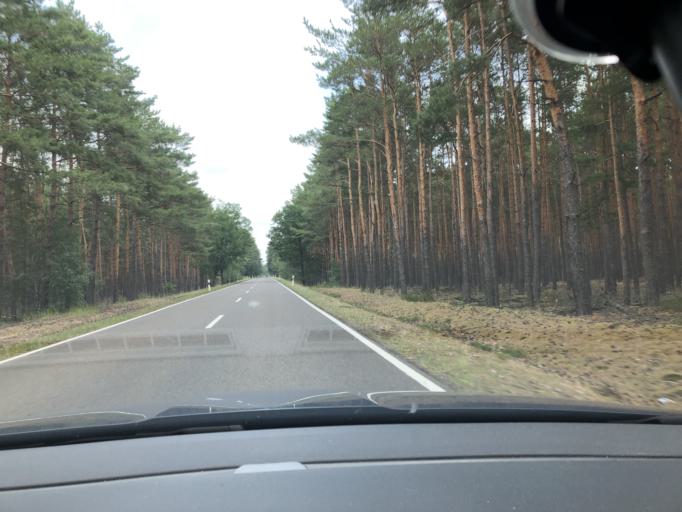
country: DE
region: Brandenburg
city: Schlepzig
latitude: 52.0079
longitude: 13.7957
